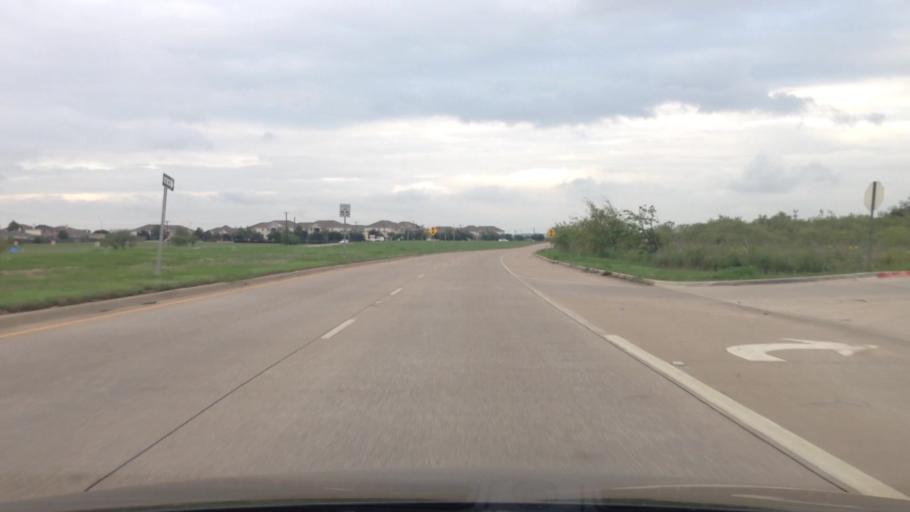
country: US
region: Texas
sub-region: Tarrant County
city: Crowley
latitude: 32.5765
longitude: -97.3334
